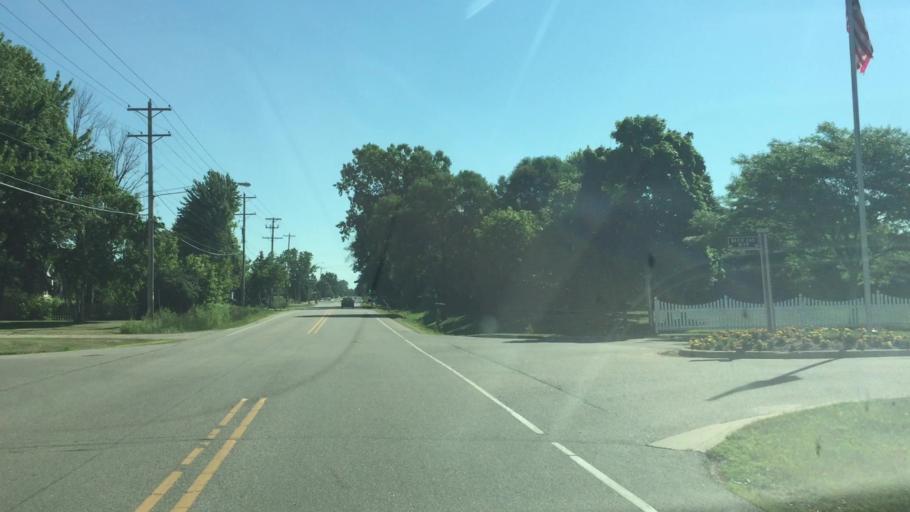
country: US
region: Wisconsin
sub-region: Winnebago County
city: Menasha
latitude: 44.2173
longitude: -88.4070
